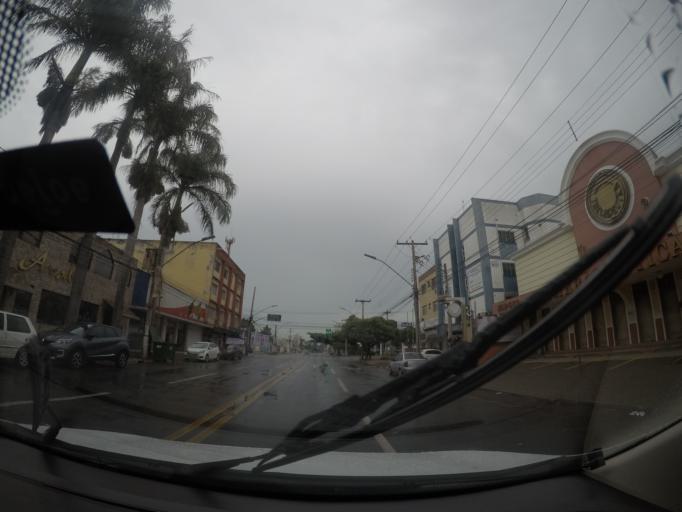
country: BR
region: Goias
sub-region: Goiania
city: Goiania
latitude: -16.6824
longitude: -49.2530
